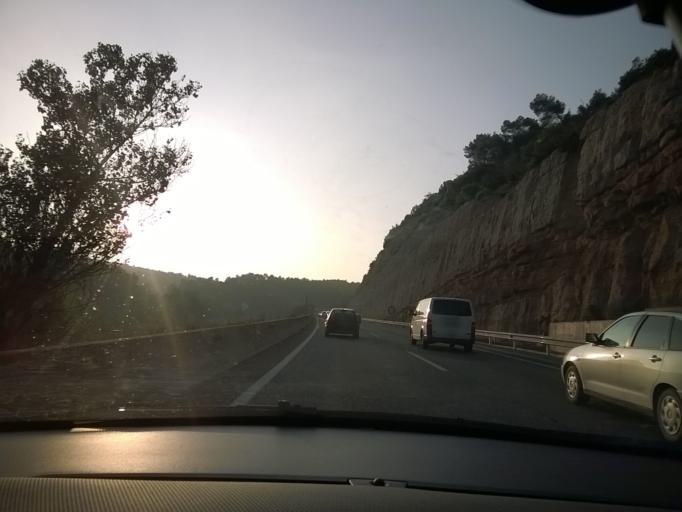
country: ES
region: Catalonia
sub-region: Provincia de Barcelona
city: Castelloli
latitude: 41.5956
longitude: 1.7455
